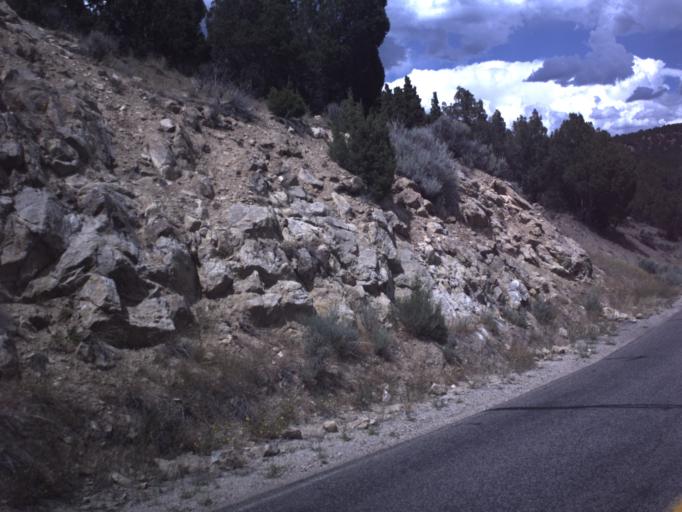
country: US
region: Utah
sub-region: Summit County
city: Oakley
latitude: 40.7652
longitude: -111.3838
